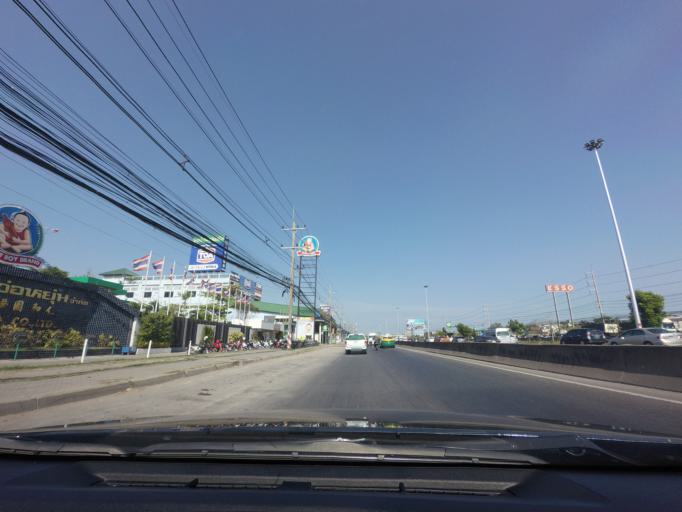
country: TH
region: Samut Sakhon
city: Samut Sakhon
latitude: 13.5433
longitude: 100.2418
